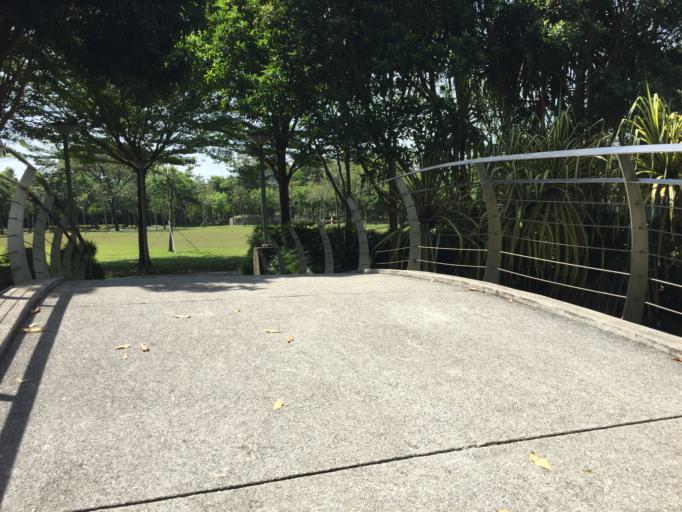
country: MY
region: Kuala Lumpur
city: Kuala Lumpur
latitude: 3.1858
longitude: 101.6321
